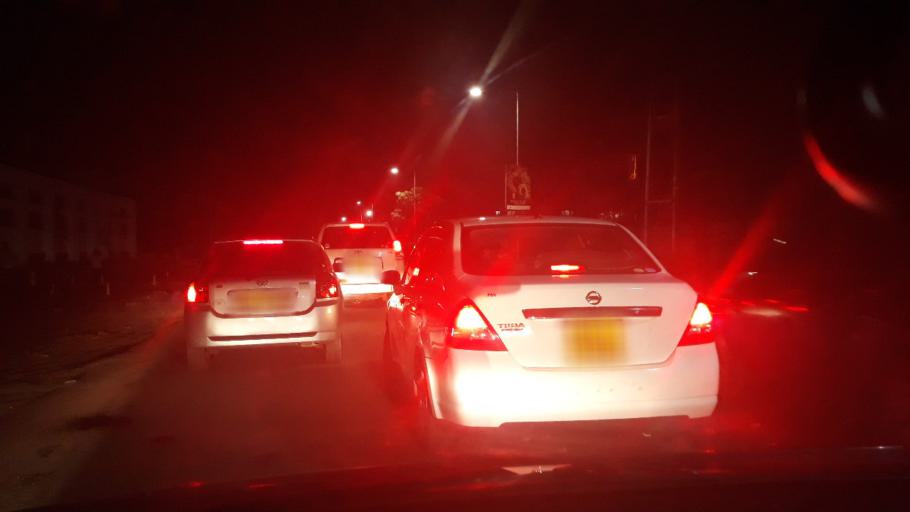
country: KE
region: Nairobi Area
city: Pumwani
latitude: -1.2959
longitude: 36.8350
